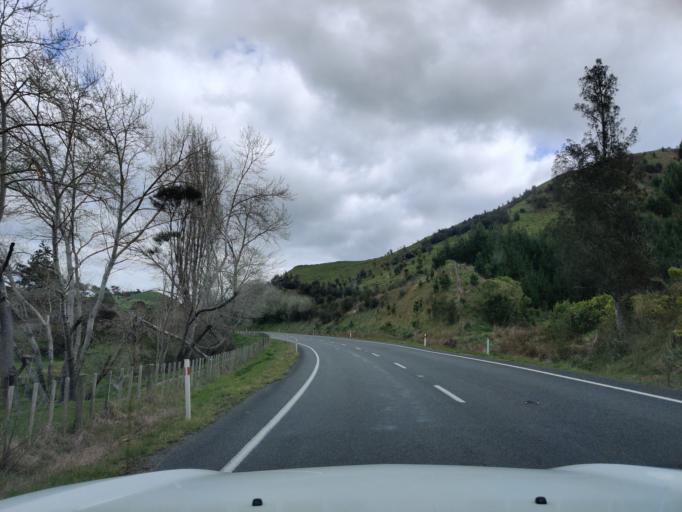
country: NZ
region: Manawatu-Wanganui
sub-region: Wanganui District
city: Wanganui
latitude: -39.8451
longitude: 175.1459
